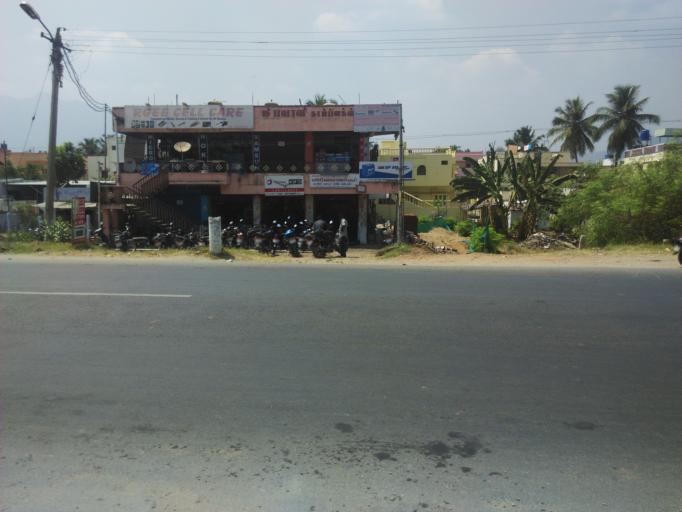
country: IN
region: Tamil Nadu
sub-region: Coimbatore
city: Periyanayakkanpalaiyam
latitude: 11.1547
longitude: 76.9443
